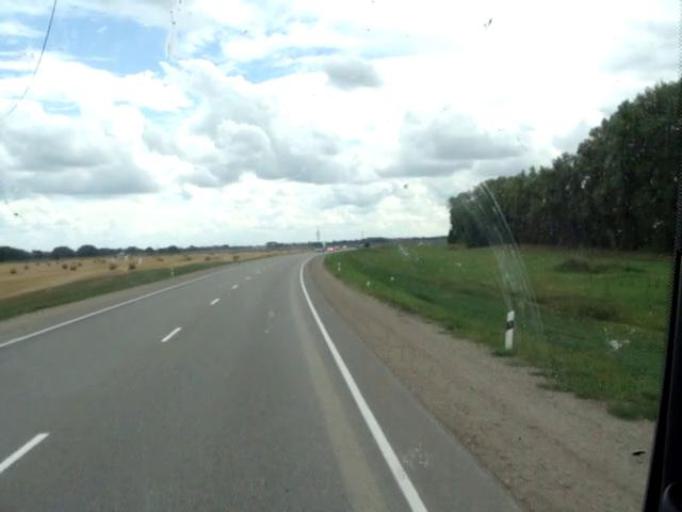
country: RU
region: Altai Krai
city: Shubenka
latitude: 52.6832
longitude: 85.0451
